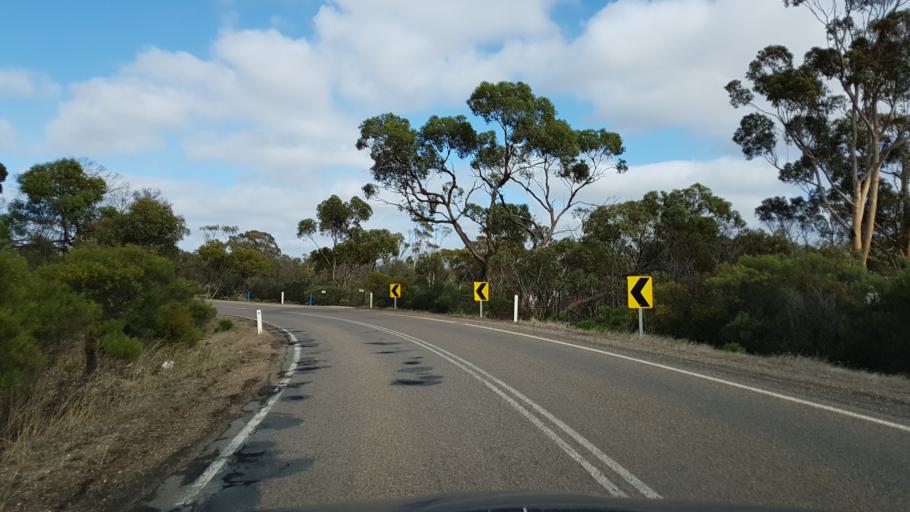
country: AU
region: South Australia
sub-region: Murray Bridge
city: Murray Bridge
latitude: -35.1121
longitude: 139.2241
